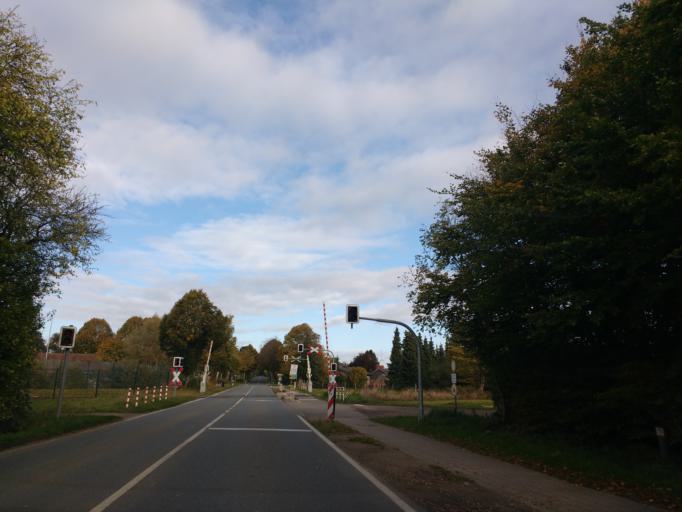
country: DE
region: Schleswig-Holstein
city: Altenkrempe
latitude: 54.1386
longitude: 10.8239
